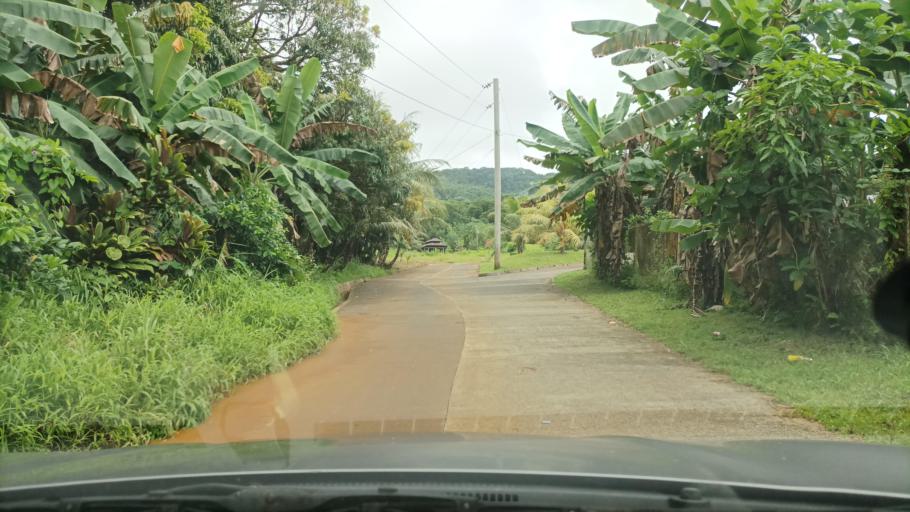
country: FM
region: Pohnpei
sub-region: Madolenihm Municipality
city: Madolenihm Municipality Government
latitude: 6.8877
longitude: 158.2919
